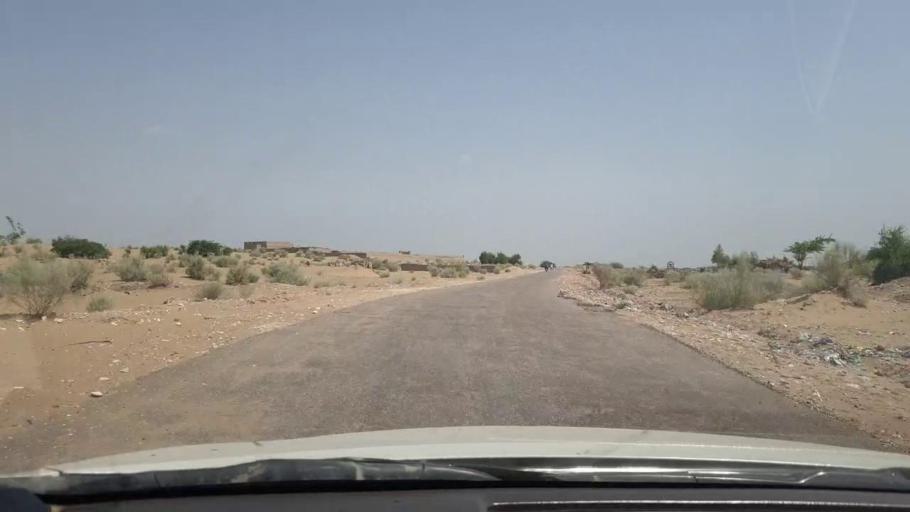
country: PK
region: Sindh
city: Rohri
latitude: 27.4918
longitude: 69.0504
